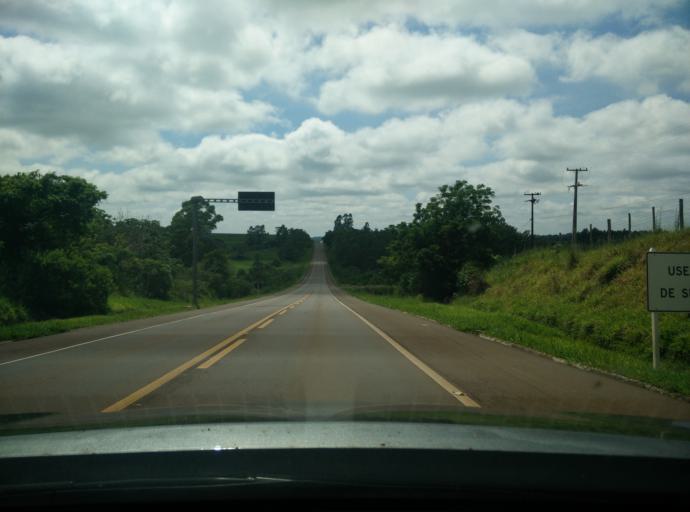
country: BR
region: Parana
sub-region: Campo Mourao
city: Campo Mourao
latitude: -23.9742
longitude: -52.5527
